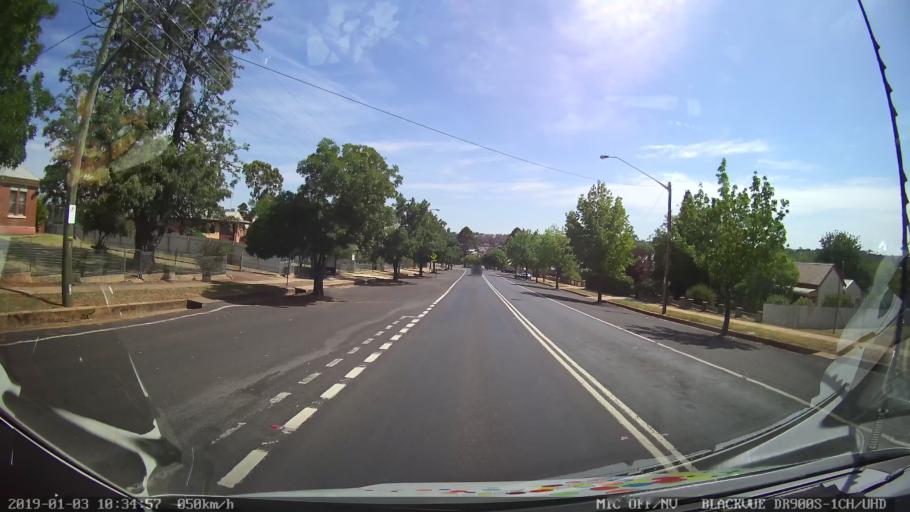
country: AU
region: New South Wales
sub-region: Young
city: Young
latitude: -34.3183
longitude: 148.2927
